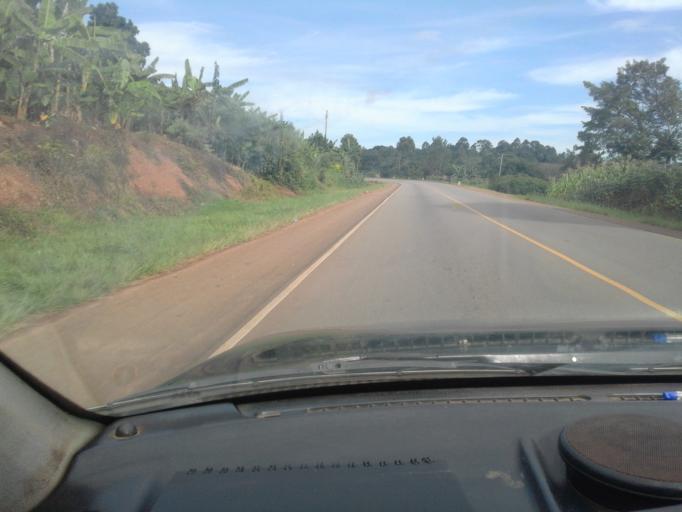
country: UG
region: Central Region
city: Masaka
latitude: -0.3453
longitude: 31.6226
